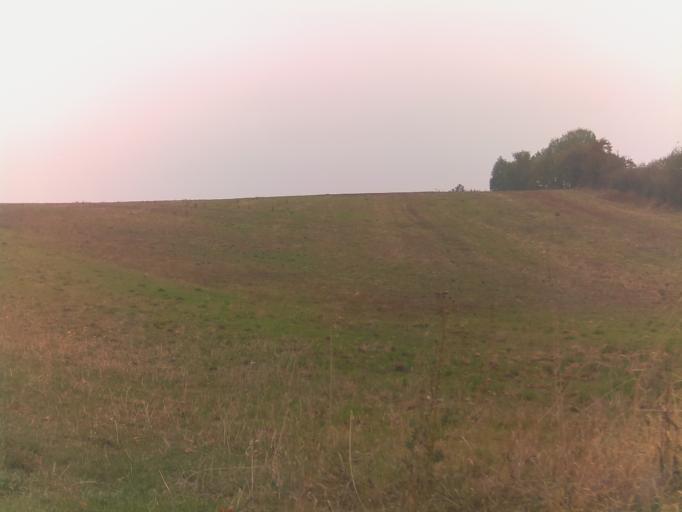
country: DE
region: Thuringia
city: Oberhain
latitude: 50.6403
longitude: 11.1197
